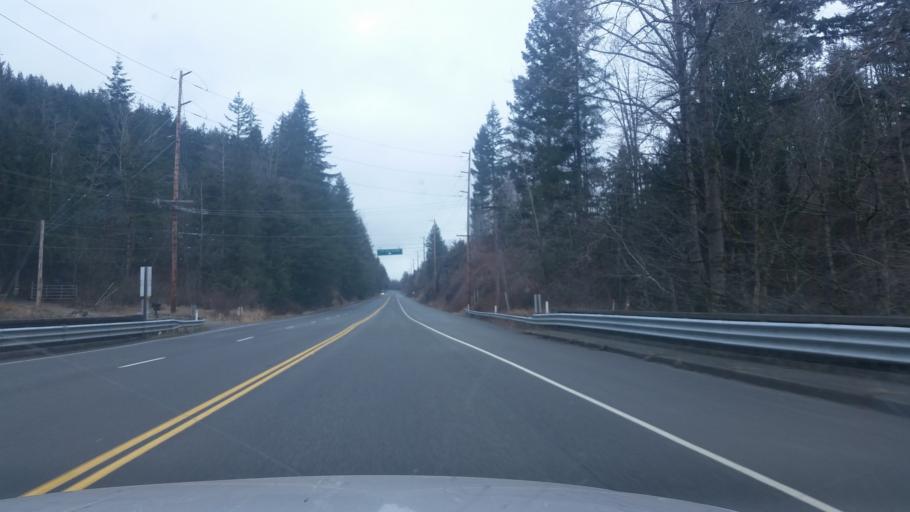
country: US
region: Washington
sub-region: King County
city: Snoqualmie
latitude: 47.5097
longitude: -121.8194
